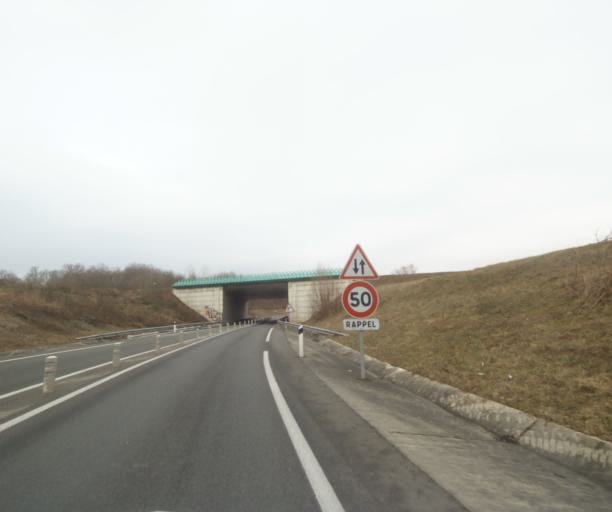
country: FR
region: Champagne-Ardenne
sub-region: Departement de la Haute-Marne
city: Bettancourt-la-Ferree
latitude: 48.6201
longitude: 4.9843
